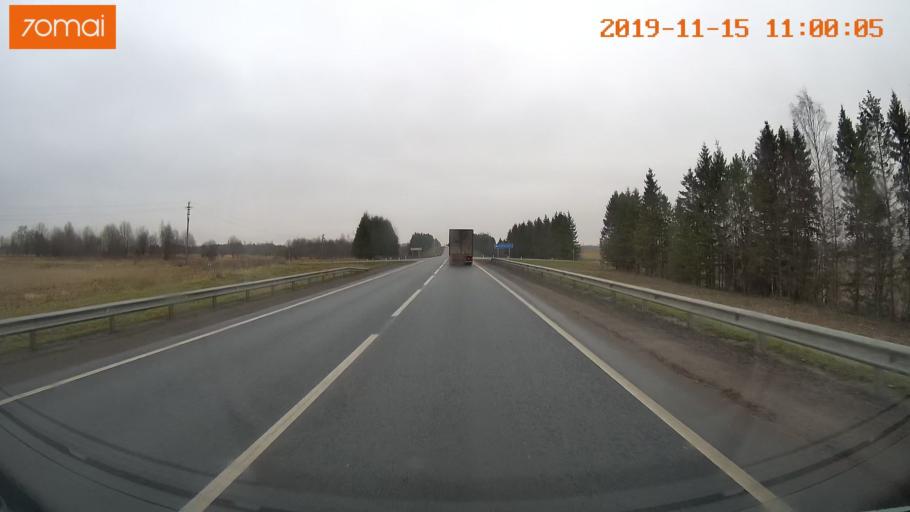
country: RU
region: Vologda
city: Chebsara
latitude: 59.1386
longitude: 38.8918
